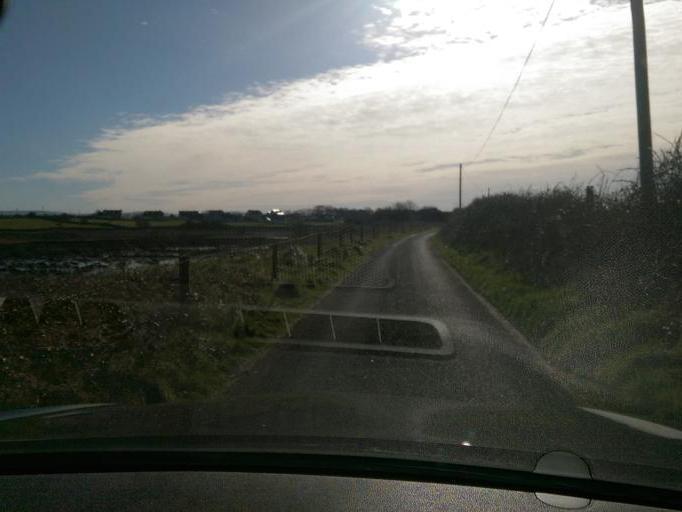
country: IE
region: Connaught
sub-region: County Galway
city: Oranmore
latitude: 53.2391
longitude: -8.9646
